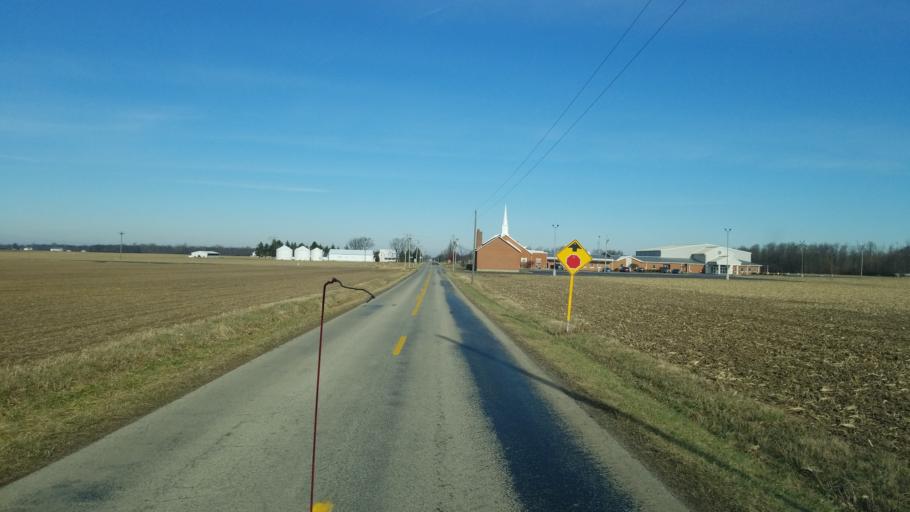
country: US
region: Ohio
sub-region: Allen County
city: Bluffton
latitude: 40.8892
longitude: -83.9383
